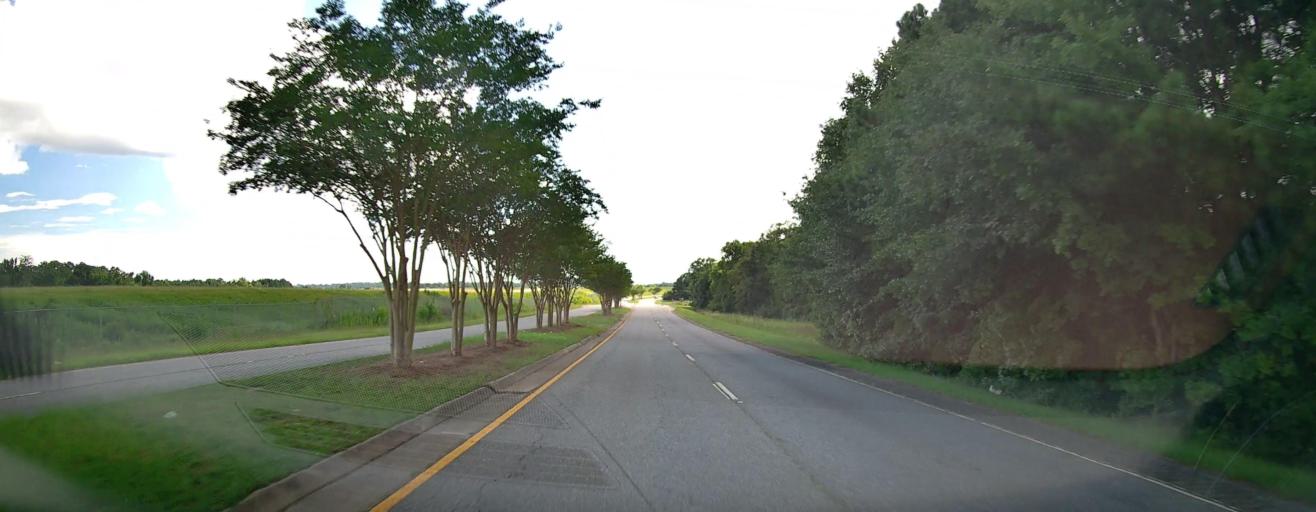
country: US
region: Georgia
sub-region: Muscogee County
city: Columbus
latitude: 32.5218
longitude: -84.9316
